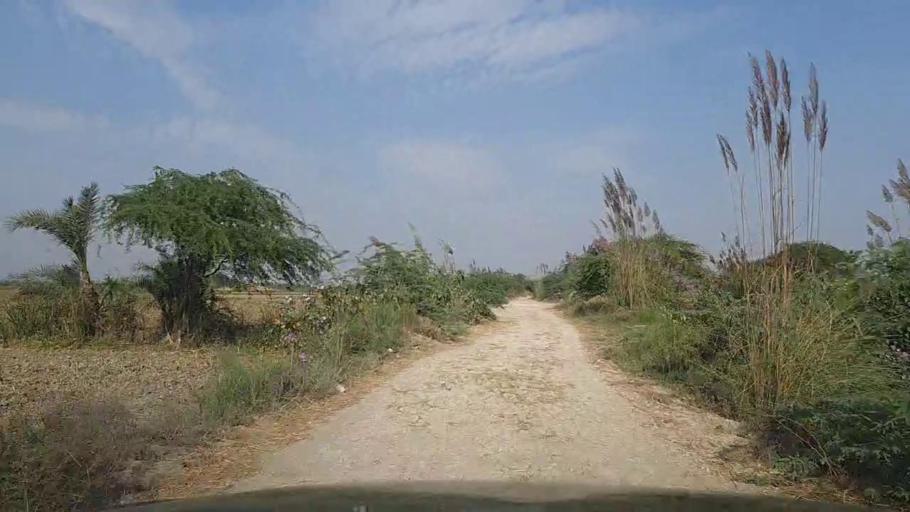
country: PK
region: Sindh
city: Thatta
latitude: 24.7680
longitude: 67.7717
